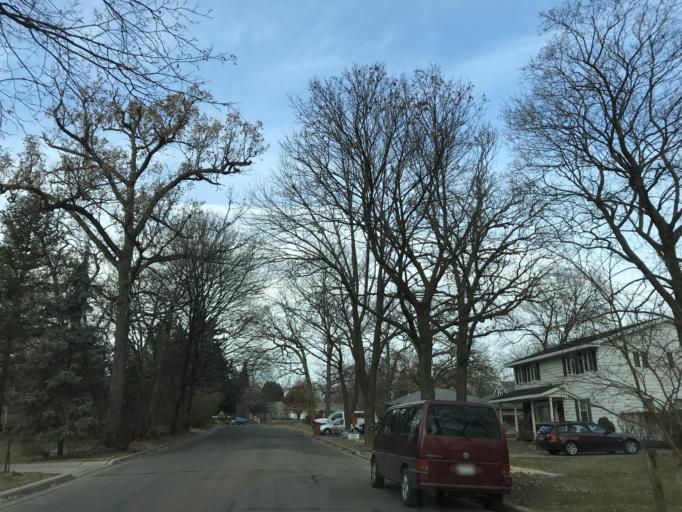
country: US
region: Wisconsin
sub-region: Dane County
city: Monona
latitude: 43.0685
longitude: -89.3384
